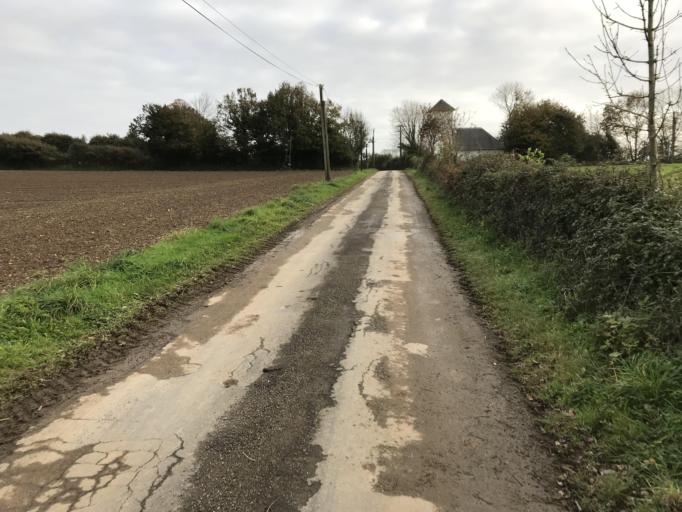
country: FR
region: Brittany
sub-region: Departement du Finistere
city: Hopital-Camfrout
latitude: 48.3269
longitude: -4.2051
